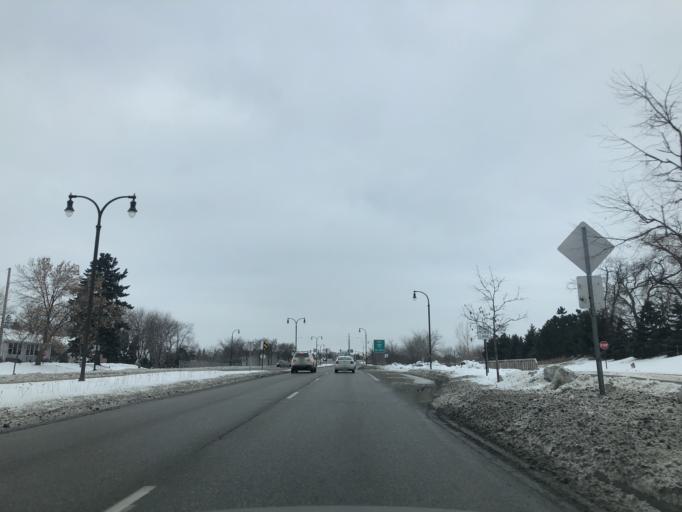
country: US
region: Minnesota
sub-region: Hennepin County
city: Robbinsdale
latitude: 45.0336
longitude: -93.3398
